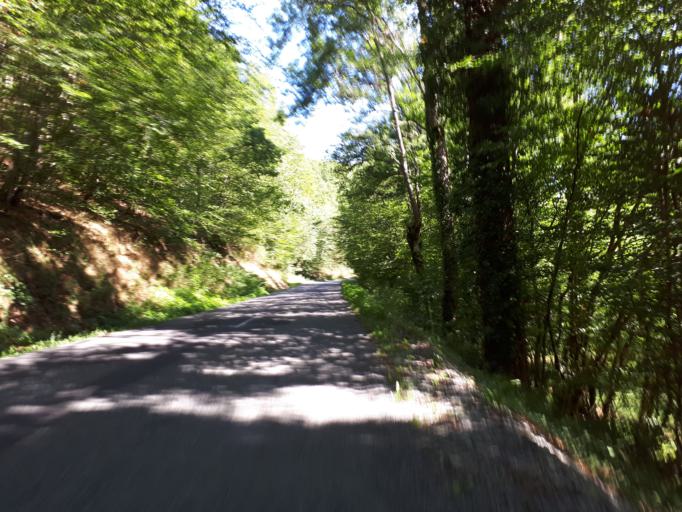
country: FR
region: Rhone-Alpes
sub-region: Departement de la Loire
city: Pouilly-les-Feurs
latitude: 45.8161
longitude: 4.2461
